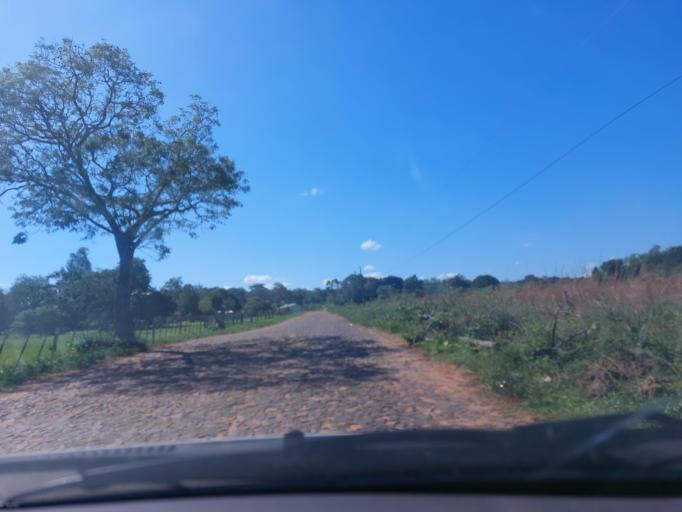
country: PY
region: San Pedro
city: Itacurubi del Rosario
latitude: -24.5850
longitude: -56.6005
